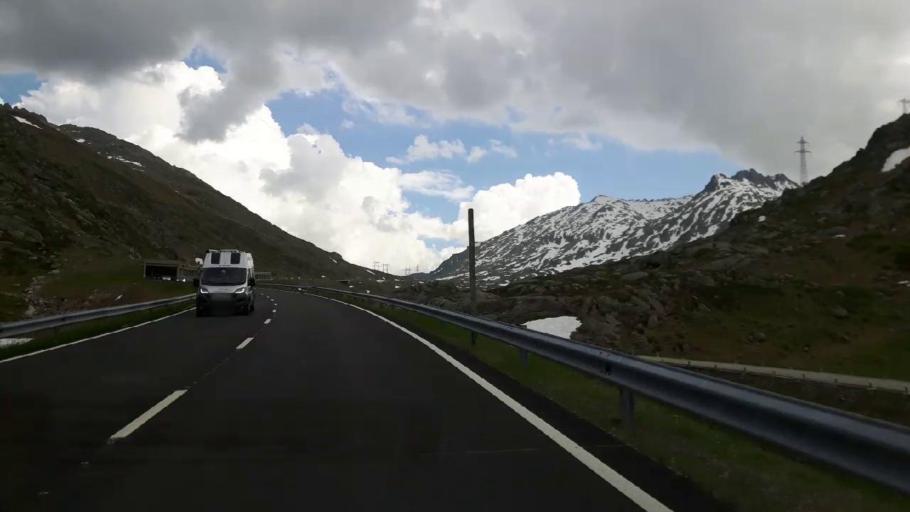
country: CH
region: Uri
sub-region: Uri
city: Andermatt
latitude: 46.5790
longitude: 8.5587
